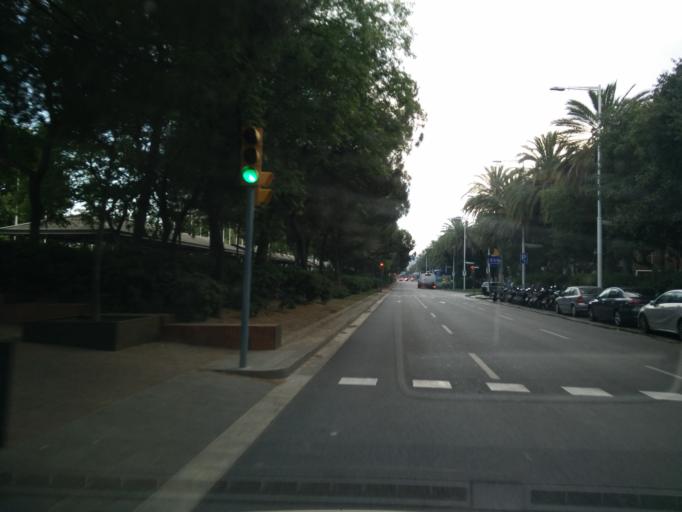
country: ES
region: Catalonia
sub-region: Provincia de Barcelona
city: Ciutat Vella
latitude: 41.3902
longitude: 2.1990
